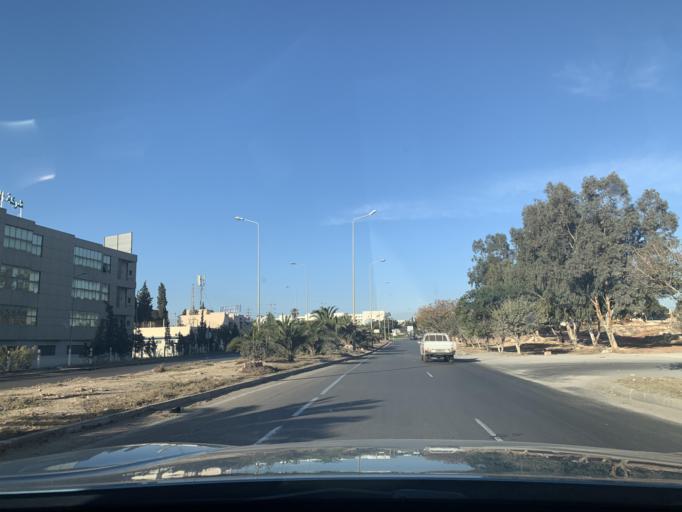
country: DZ
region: Souk Ahras
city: Souk Ahras
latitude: 36.3632
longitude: 8.0086
